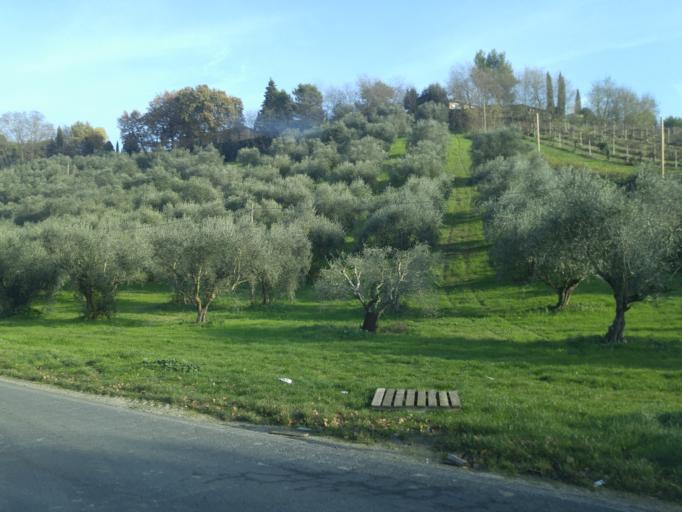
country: IT
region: The Marches
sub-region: Provincia di Pesaro e Urbino
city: Villanova
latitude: 43.7230
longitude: 12.9172
